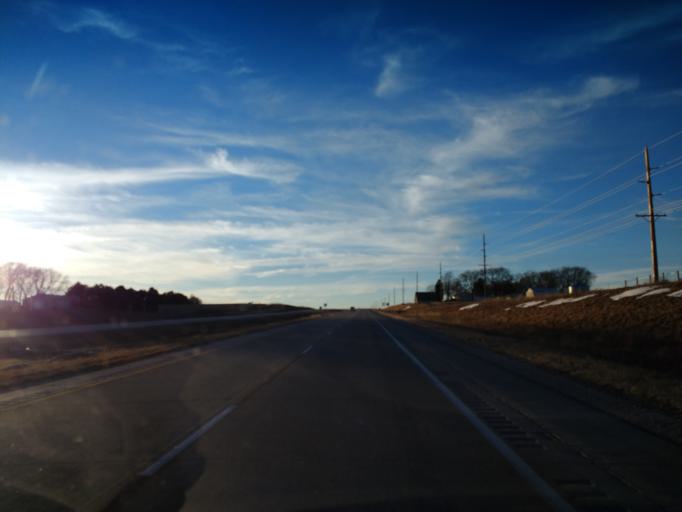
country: US
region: Iowa
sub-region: Ida County
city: Holstein
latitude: 42.4751
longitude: -95.4750
